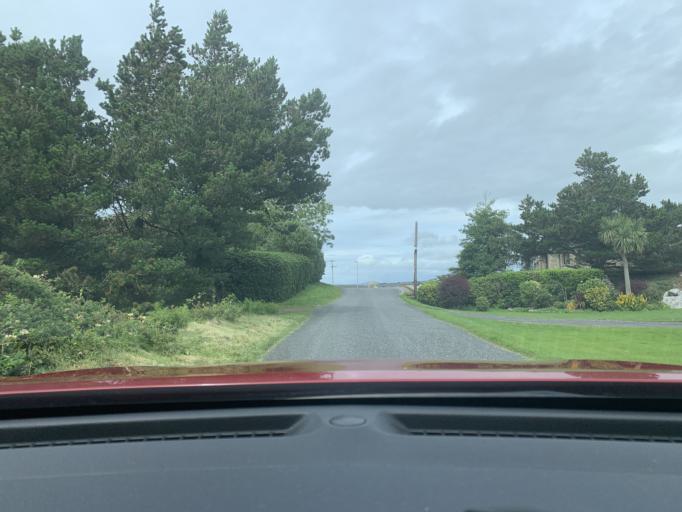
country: IE
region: Ulster
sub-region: County Donegal
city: Dungloe
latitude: 54.9430
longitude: -8.3585
